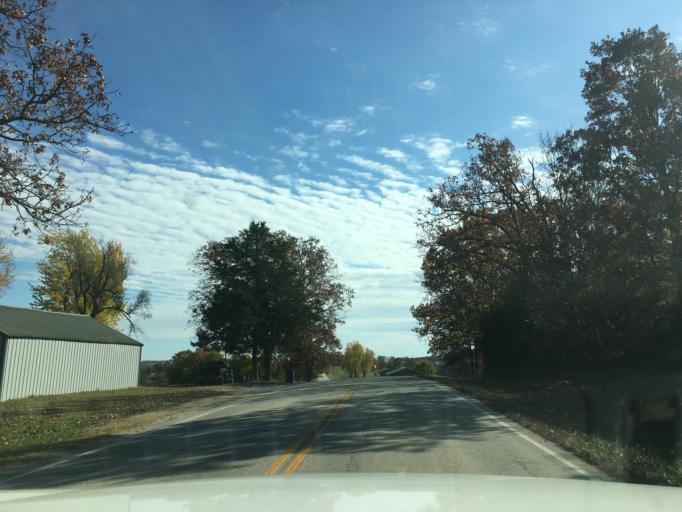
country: US
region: Missouri
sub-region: Maries County
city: Belle
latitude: 38.3529
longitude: -91.7993
